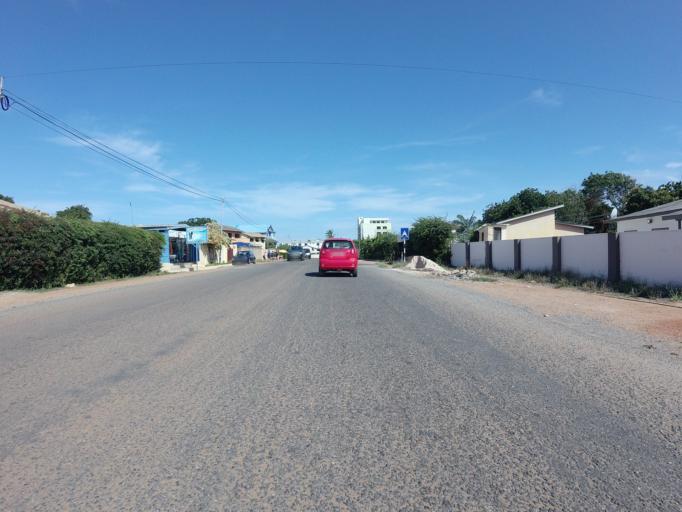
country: GH
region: Greater Accra
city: Accra
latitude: 5.5624
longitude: -0.1695
